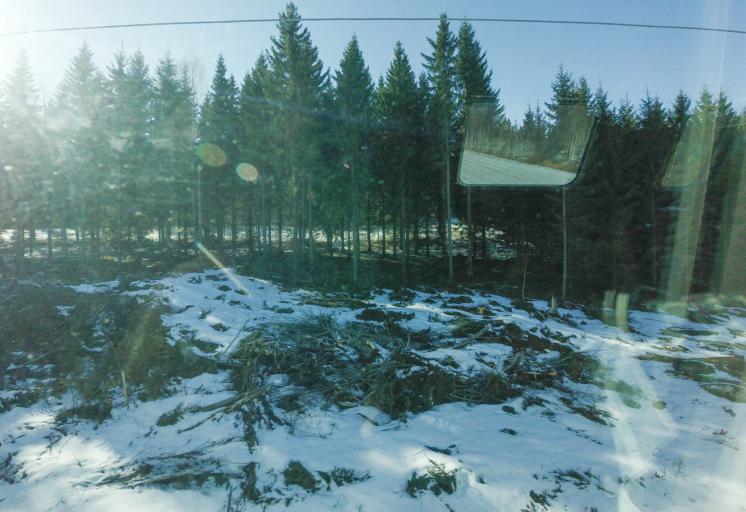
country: FI
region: South Karelia
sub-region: Imatra
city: Parikkala
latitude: 61.5135
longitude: 29.5105
